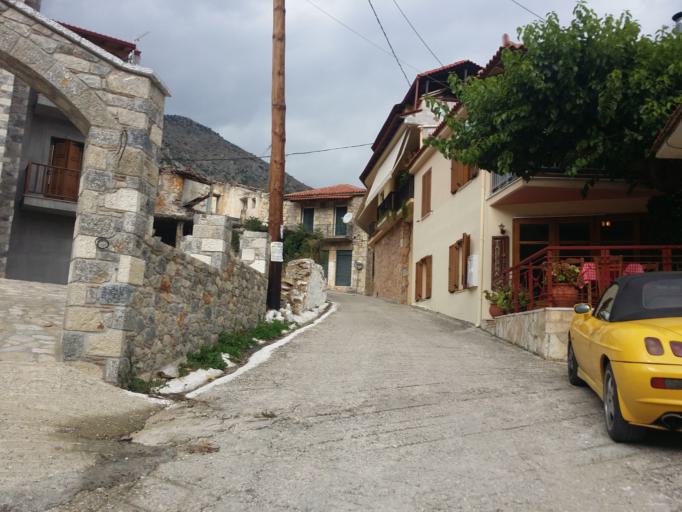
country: GR
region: Peloponnese
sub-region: Nomos Argolidos
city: Koutsopodi
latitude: 37.6395
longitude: 22.5459
